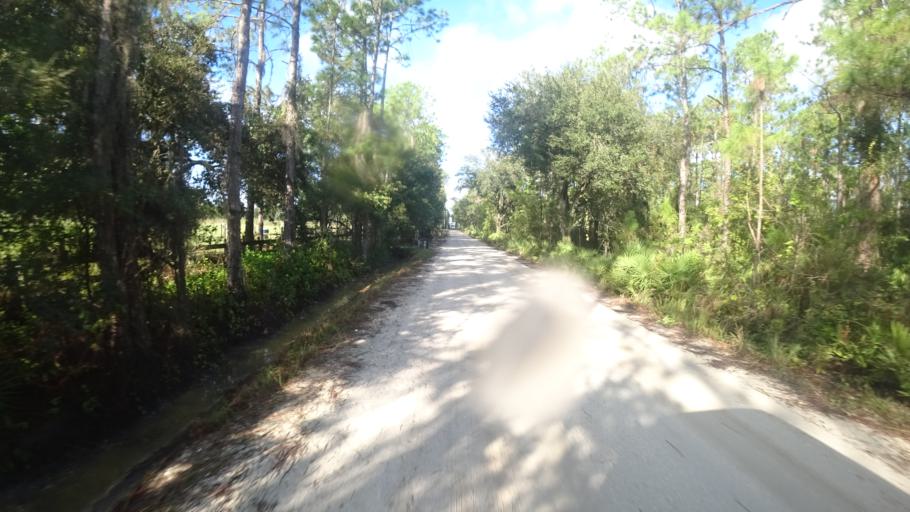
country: US
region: Florida
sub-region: Sarasota County
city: The Meadows
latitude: 27.4311
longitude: -82.3183
